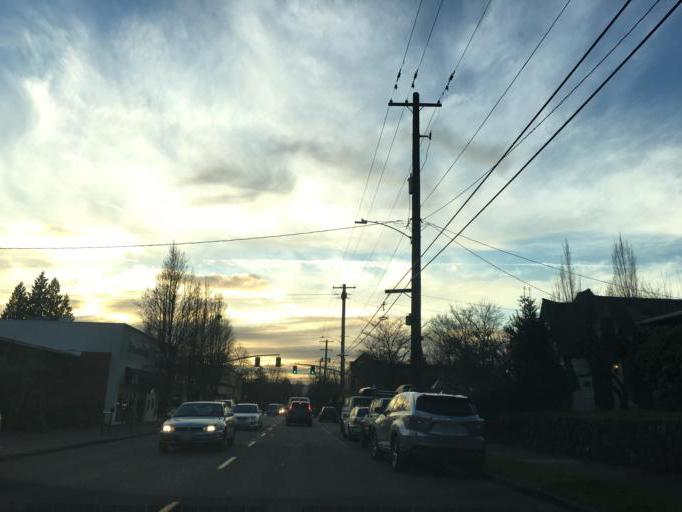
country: US
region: Oregon
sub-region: Multnomah County
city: Portland
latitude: 45.5483
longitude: -122.6400
